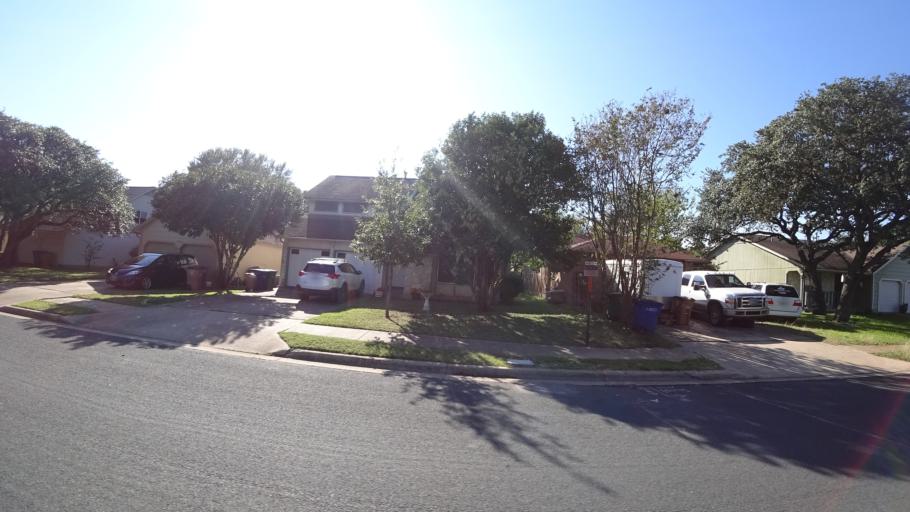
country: US
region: Texas
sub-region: Travis County
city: Shady Hollow
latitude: 30.2104
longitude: -97.8493
